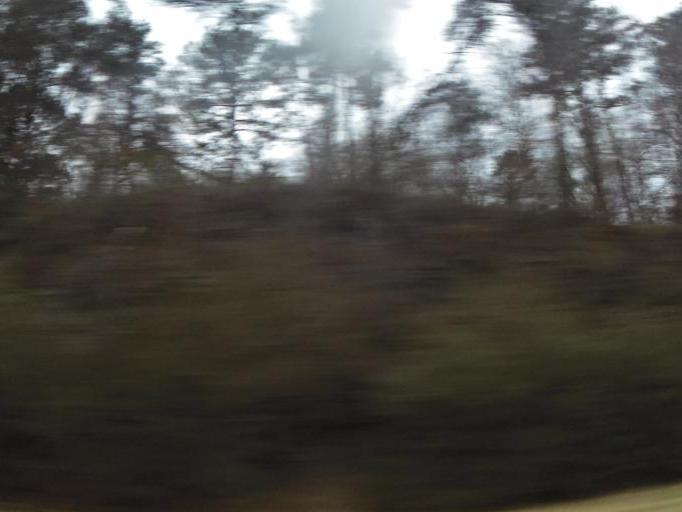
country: US
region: Alabama
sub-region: Blount County
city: Smoke Rise
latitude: 33.9755
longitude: -86.8615
